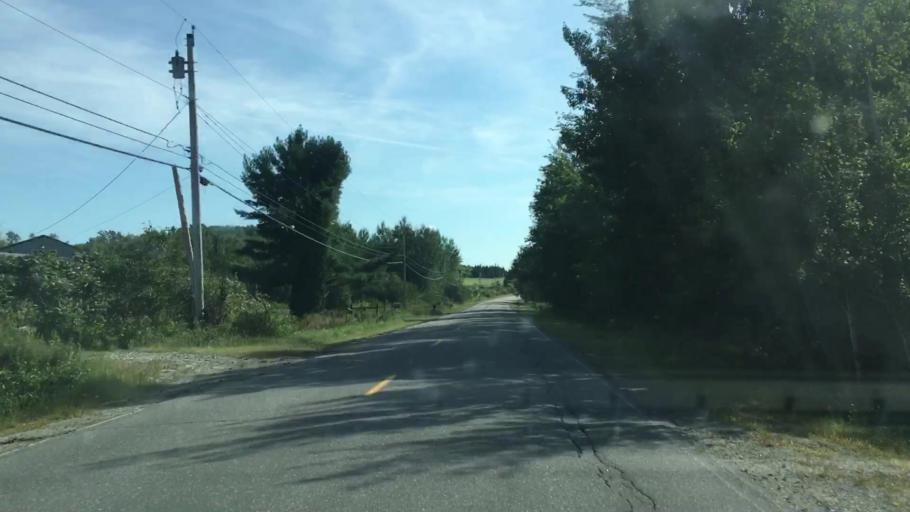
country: US
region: Maine
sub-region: Penobscot County
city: Lincoln
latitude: 45.3237
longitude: -68.5328
